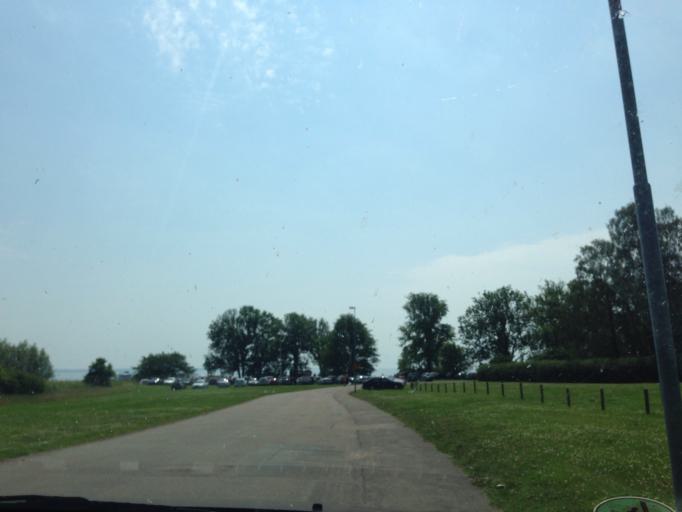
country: SE
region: Kalmar
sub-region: Kalmar Kommun
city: Kalmar
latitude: 56.6572
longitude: 16.3482
